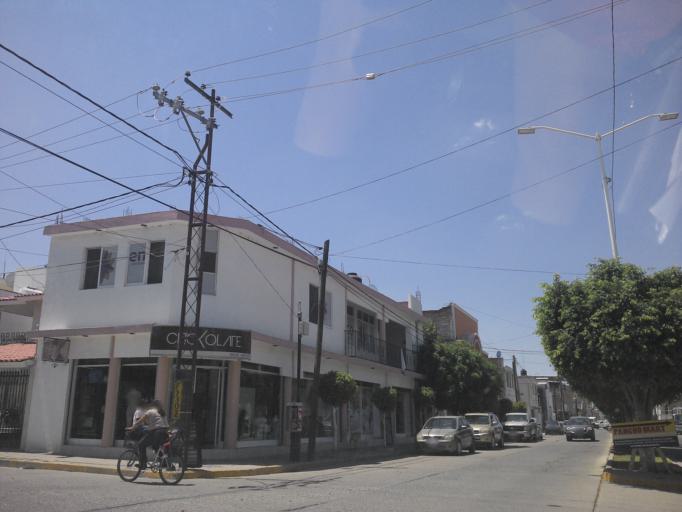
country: MX
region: Guanajuato
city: San Francisco del Rincon
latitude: 21.0123
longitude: -101.8588
